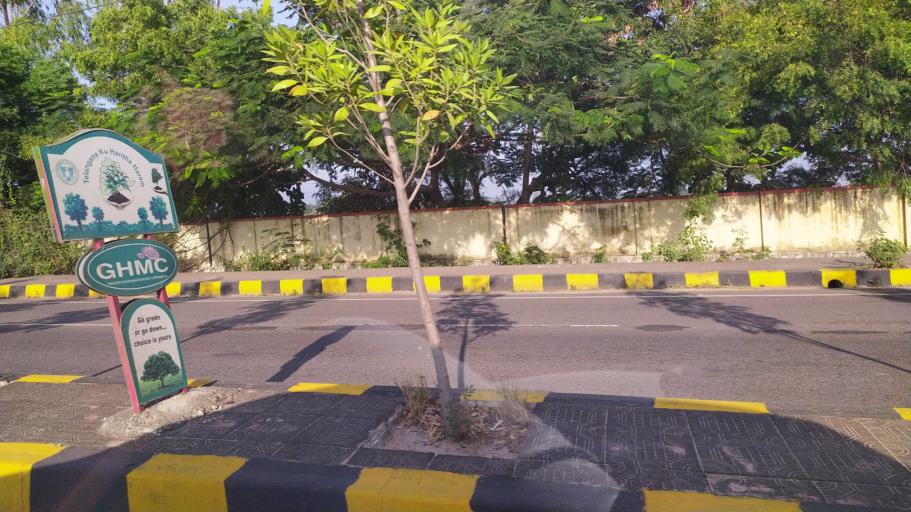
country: IN
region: Telangana
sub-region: Hyderabad
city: Hyderabad
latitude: 17.3241
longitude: 78.4059
